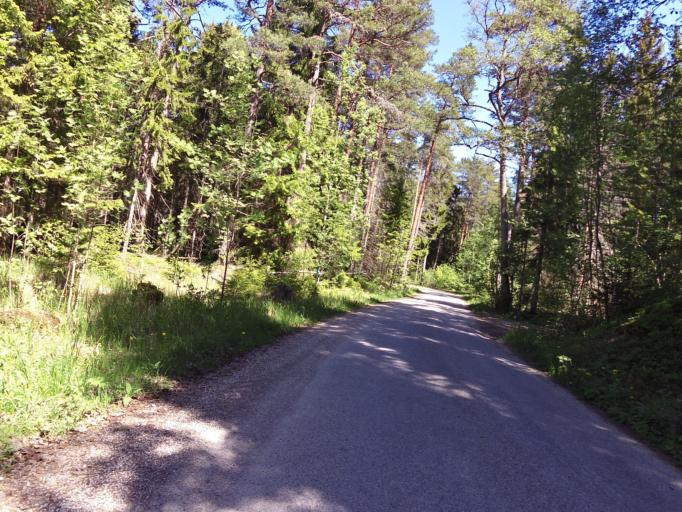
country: EE
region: Harju
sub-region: Paldiski linn
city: Paldiski
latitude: 59.2696
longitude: 23.7761
